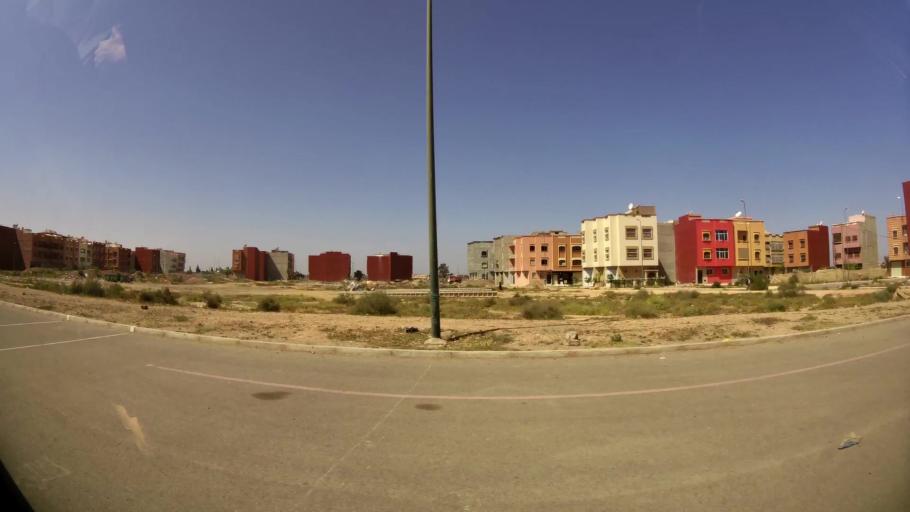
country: MA
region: Souss-Massa-Draa
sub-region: Inezgane-Ait Mellou
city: Inezgane
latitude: 30.3332
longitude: -9.5096
